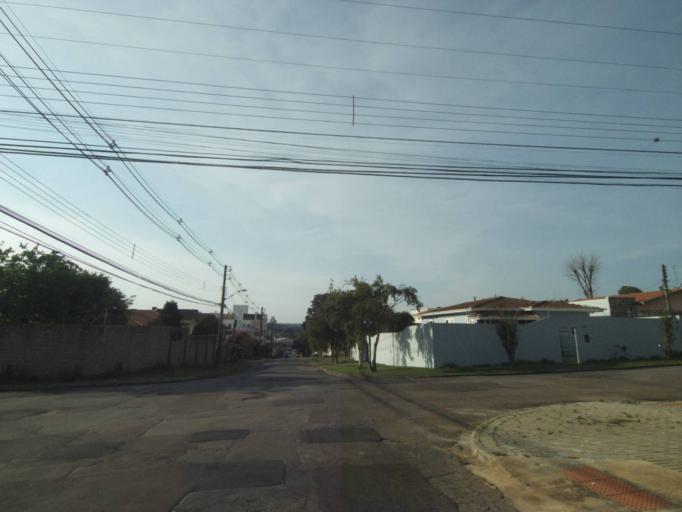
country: BR
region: Parana
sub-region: Curitiba
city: Curitiba
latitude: -25.4587
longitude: -49.3119
